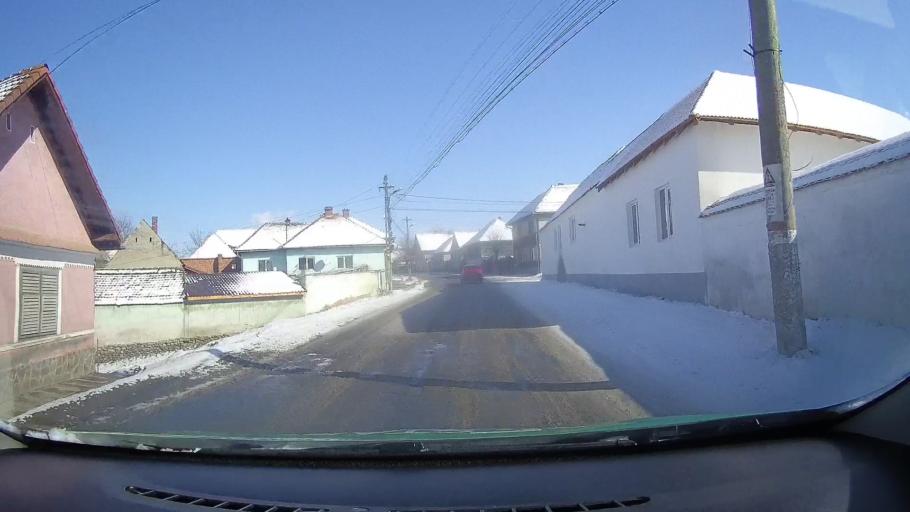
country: RO
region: Sibiu
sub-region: Comuna Avrig
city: Avrig
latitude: 45.7236
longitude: 24.3726
